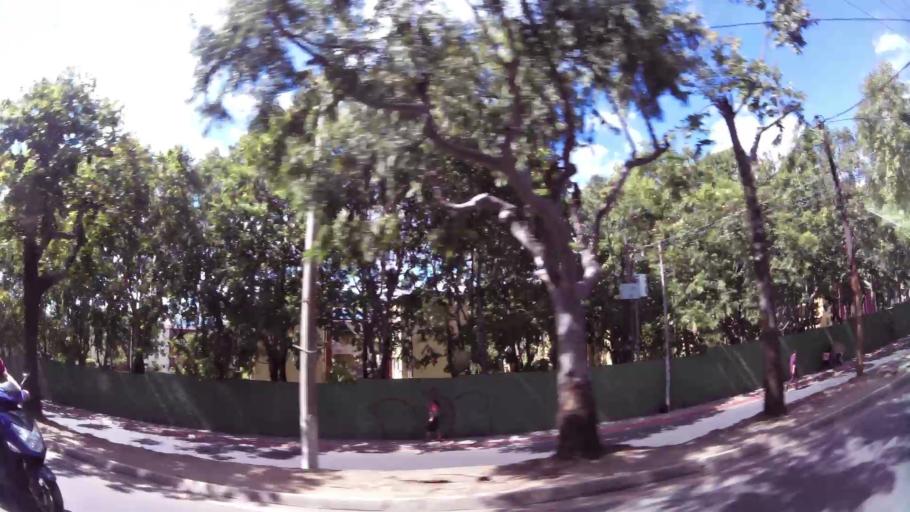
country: GT
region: Guatemala
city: Villa Nueva
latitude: 14.5477
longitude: -90.5521
